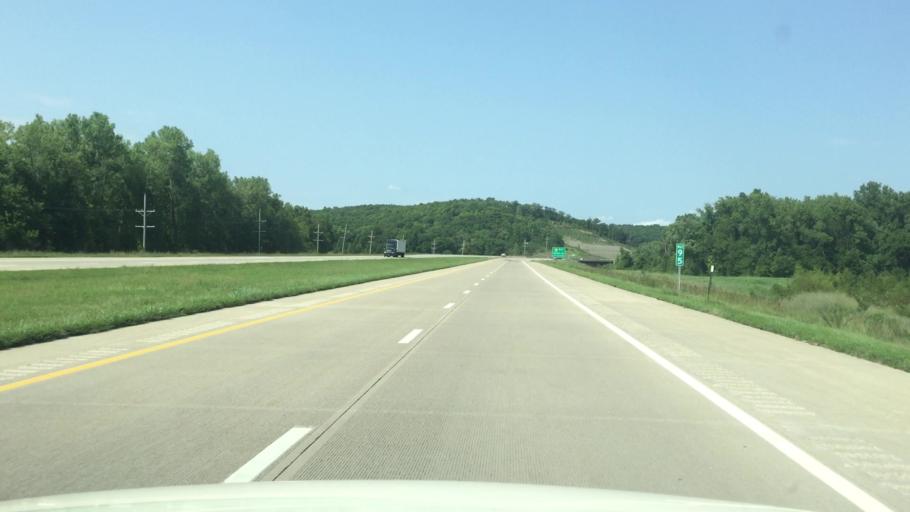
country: US
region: Kansas
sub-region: Linn County
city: Pleasanton
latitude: 38.2435
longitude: -94.6886
